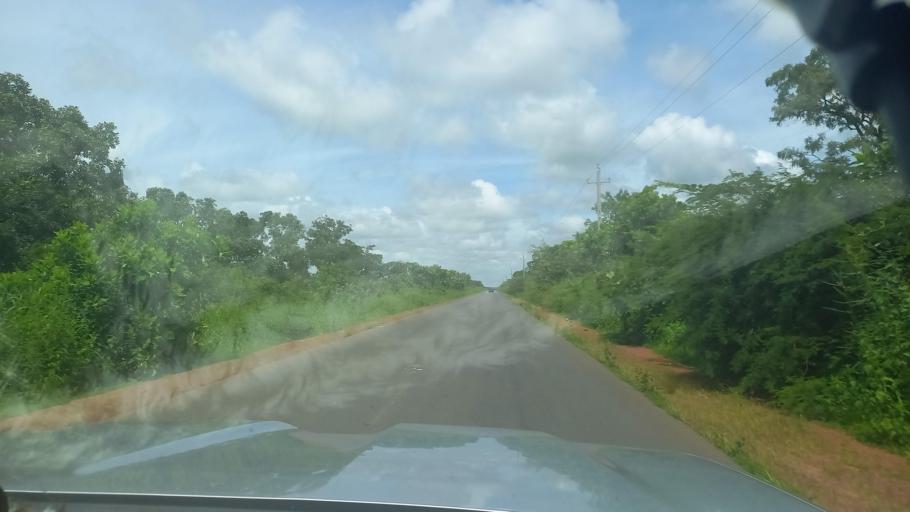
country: GM
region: Lower River
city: Kaiaf
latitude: 13.1867
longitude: -15.5581
